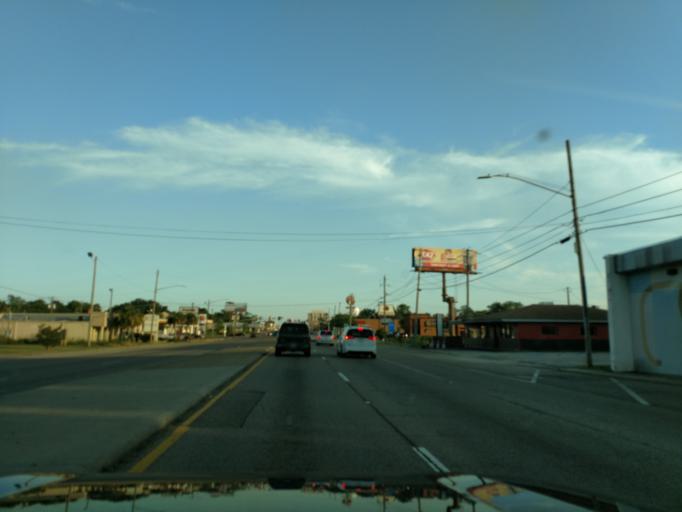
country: US
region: Mississippi
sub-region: Harrison County
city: Gulfport
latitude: 30.3823
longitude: -89.0932
